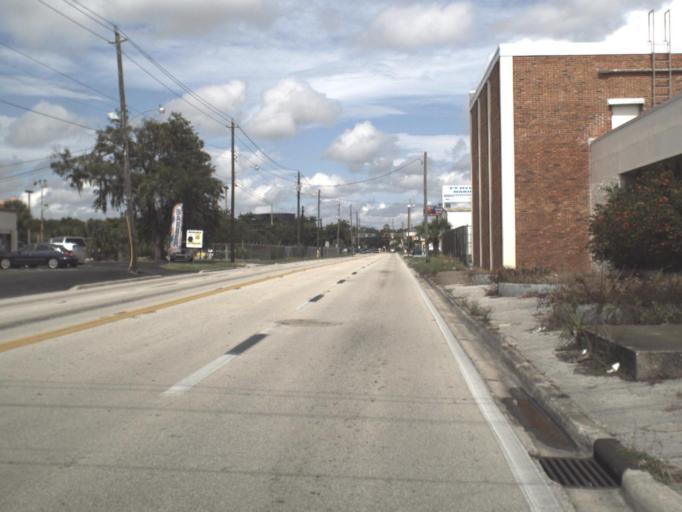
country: US
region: Florida
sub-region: Lee County
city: Fort Myers
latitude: 26.6368
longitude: -81.8623
